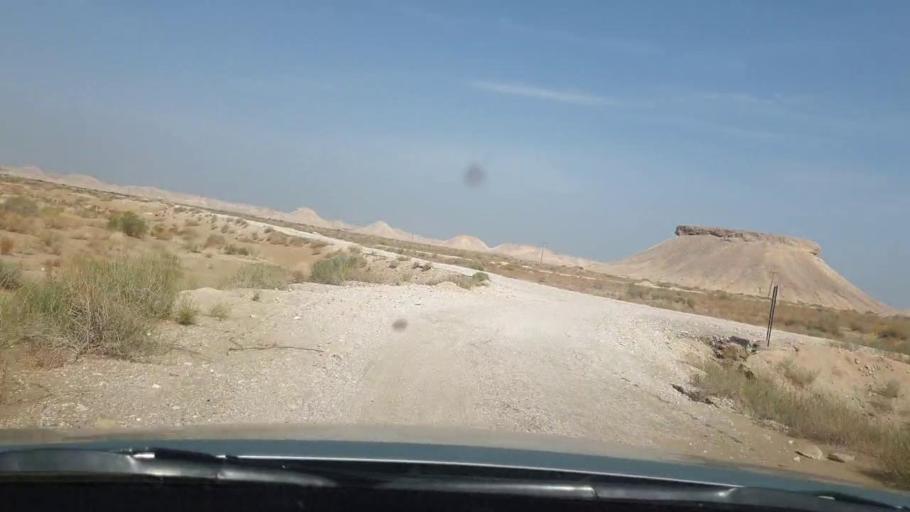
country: PK
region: Sindh
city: Kot Diji
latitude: 27.3270
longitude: 68.8096
